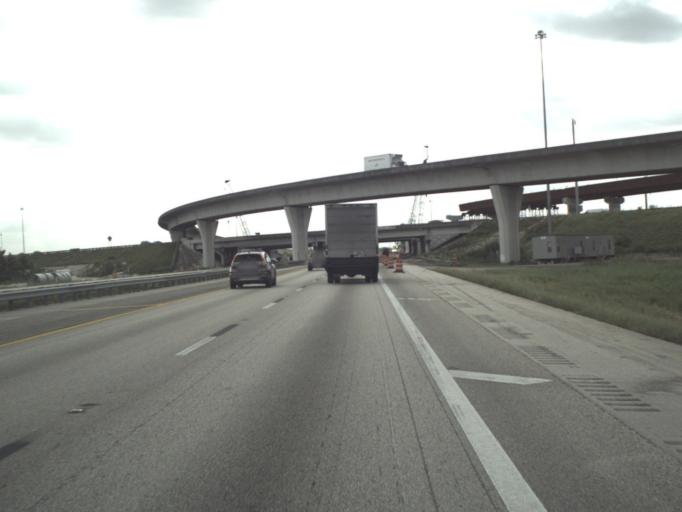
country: US
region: Florida
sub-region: Miami-Dade County
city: Palm Springs North
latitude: 25.9507
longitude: -80.3492
